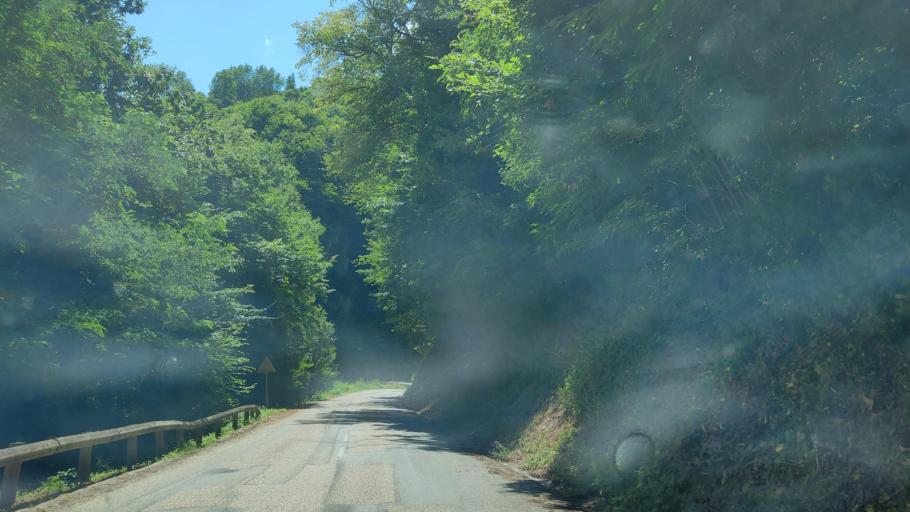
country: FR
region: Rhone-Alpes
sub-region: Departement de la Savoie
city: Saint-Remy-de-Maurienne
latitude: 45.4784
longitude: 6.2782
